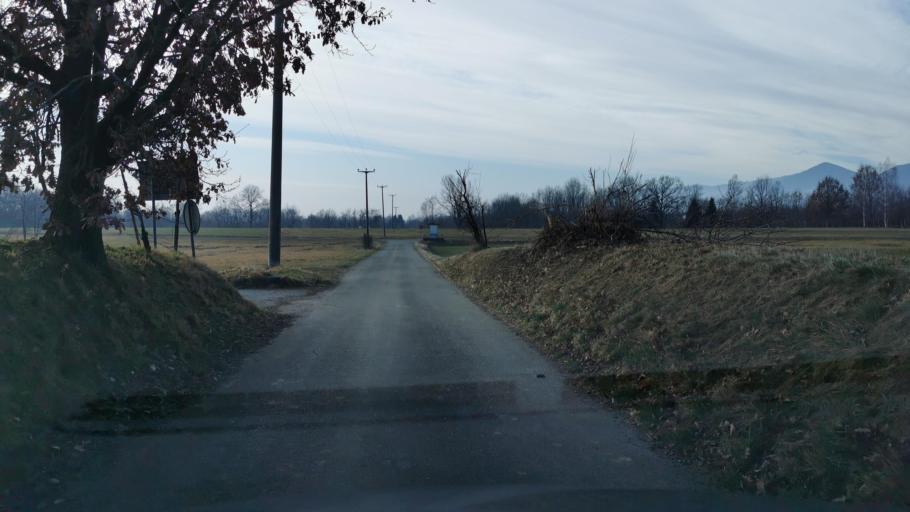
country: IT
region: Piedmont
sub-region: Provincia di Torino
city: Rocca Canavese
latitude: 45.2857
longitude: 7.5699
